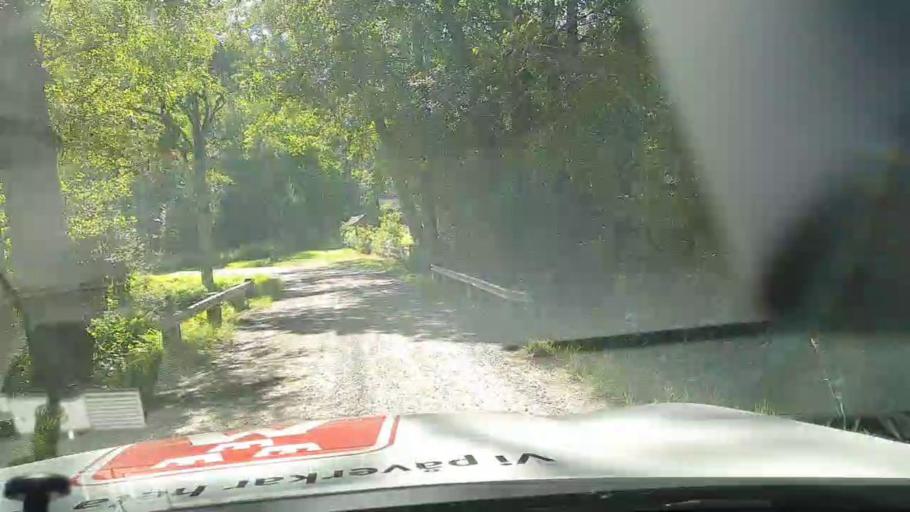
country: SE
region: Soedermanland
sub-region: Strangnas Kommun
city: Akers Styckebruk
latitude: 59.2119
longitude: 16.9108
